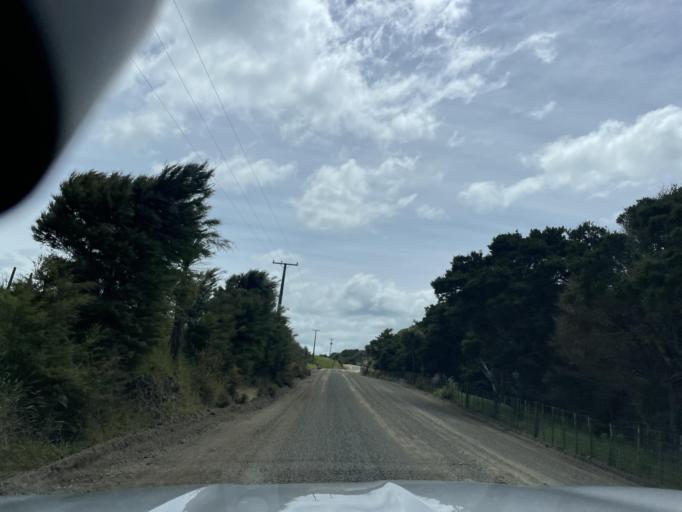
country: NZ
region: Auckland
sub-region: Auckland
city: Wellsford
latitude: -36.1563
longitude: 174.2870
